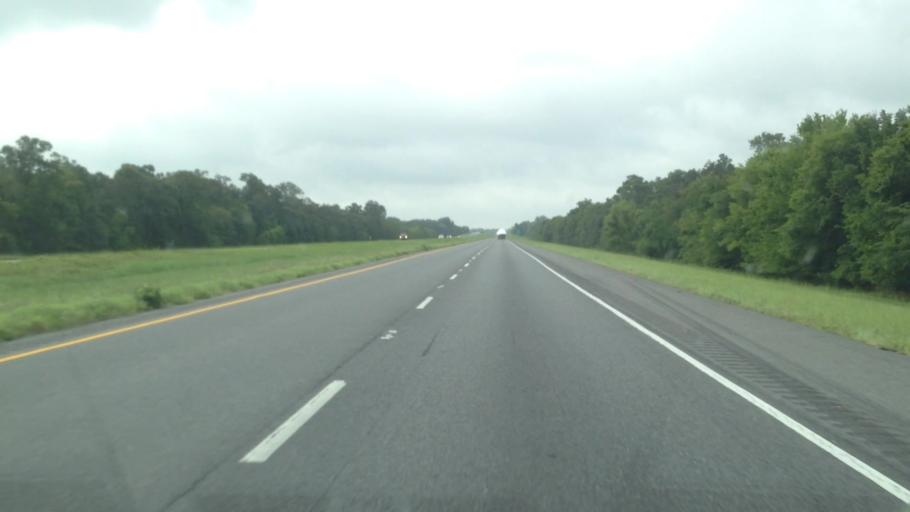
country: US
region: Louisiana
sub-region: Saint Landry Parish
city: Opelousas
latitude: 30.6622
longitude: -92.0673
